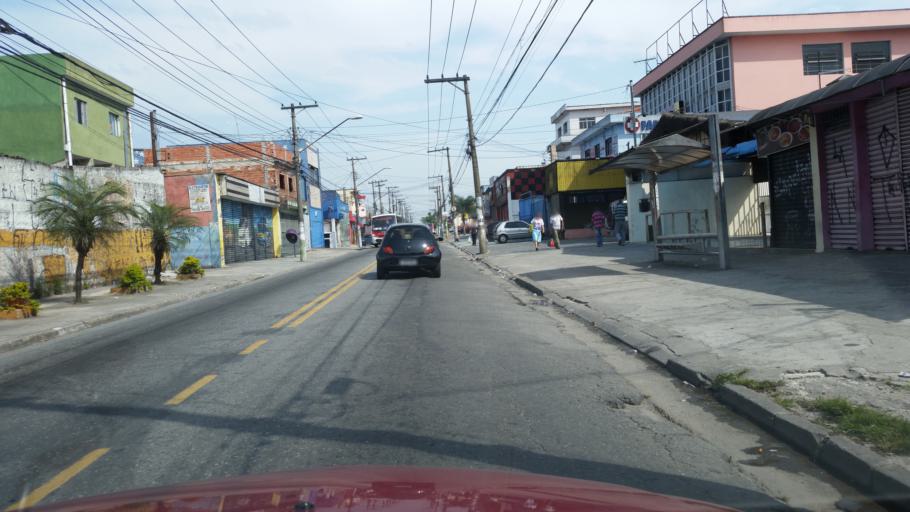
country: BR
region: Sao Paulo
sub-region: Ferraz De Vasconcelos
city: Ferraz de Vasconcelos
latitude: -23.5395
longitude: -46.4265
